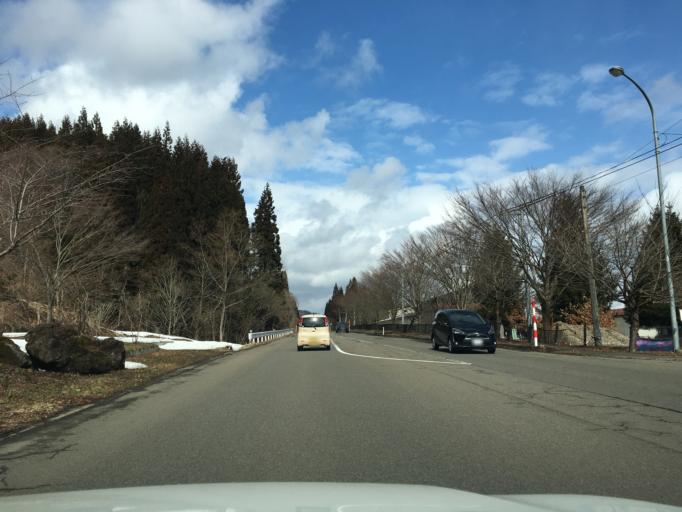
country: JP
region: Akita
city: Takanosu
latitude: 40.0190
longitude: 140.2753
